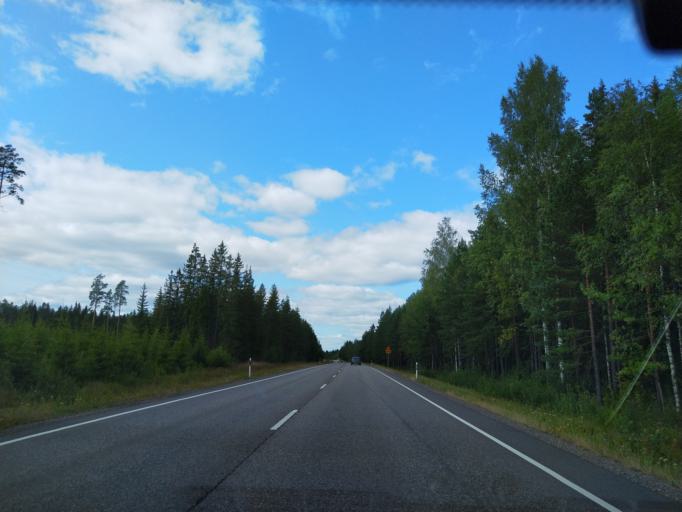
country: FI
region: Haeme
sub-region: Haemeenlinna
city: Renko
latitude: 60.7629
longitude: 24.2741
